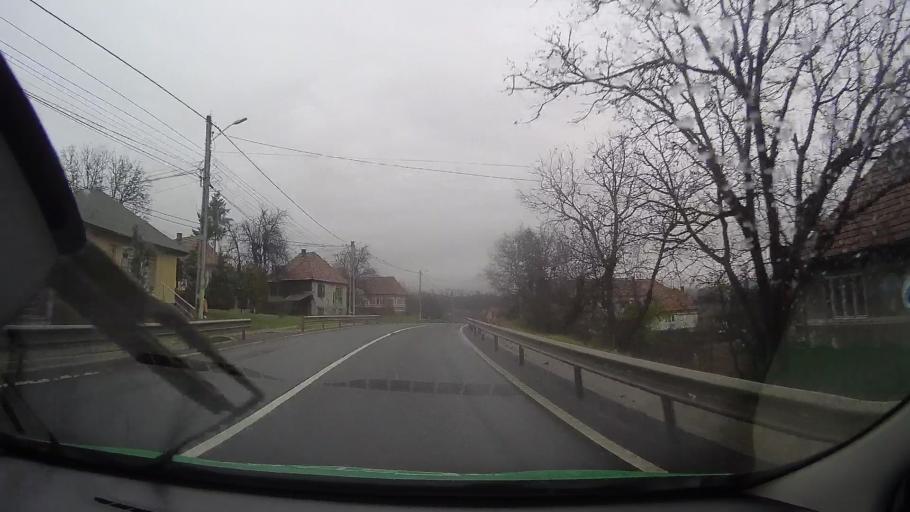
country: RO
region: Mures
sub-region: Comuna Brancovenesti
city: Brancovenesti
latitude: 46.8534
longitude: 24.7551
